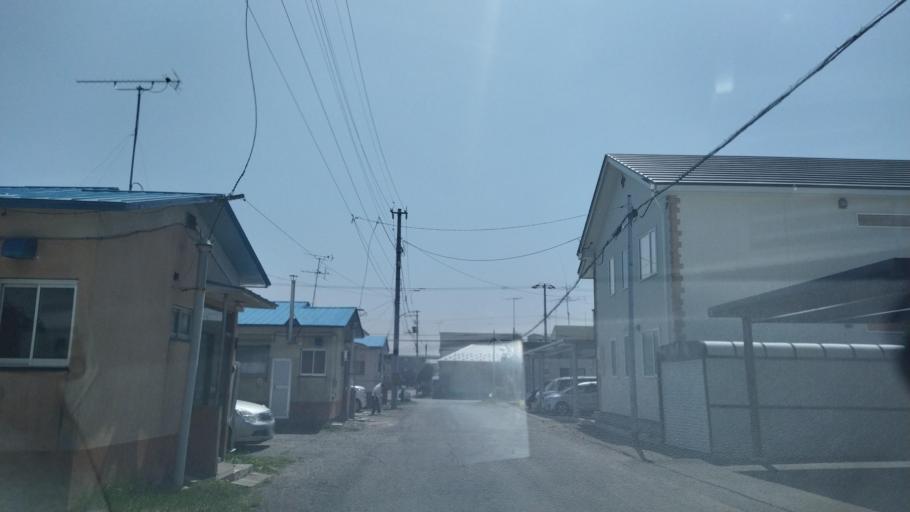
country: JP
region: Hokkaido
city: Obihiro
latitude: 42.9330
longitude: 143.1729
